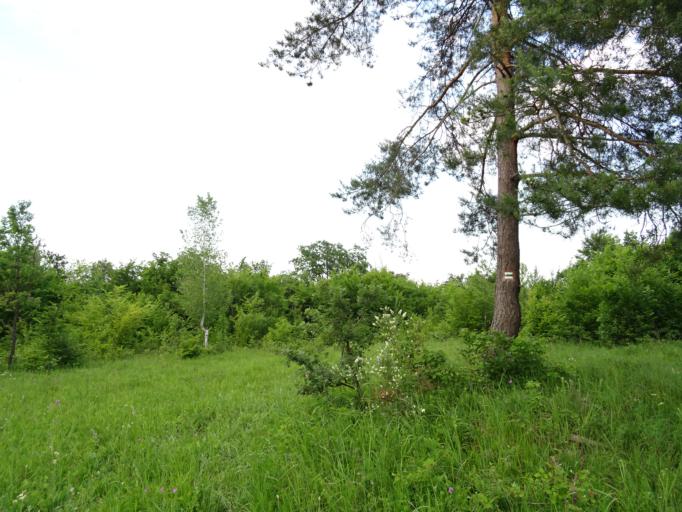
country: HU
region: Borsod-Abauj-Zemplen
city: Szendro
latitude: 48.4768
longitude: 20.6753
